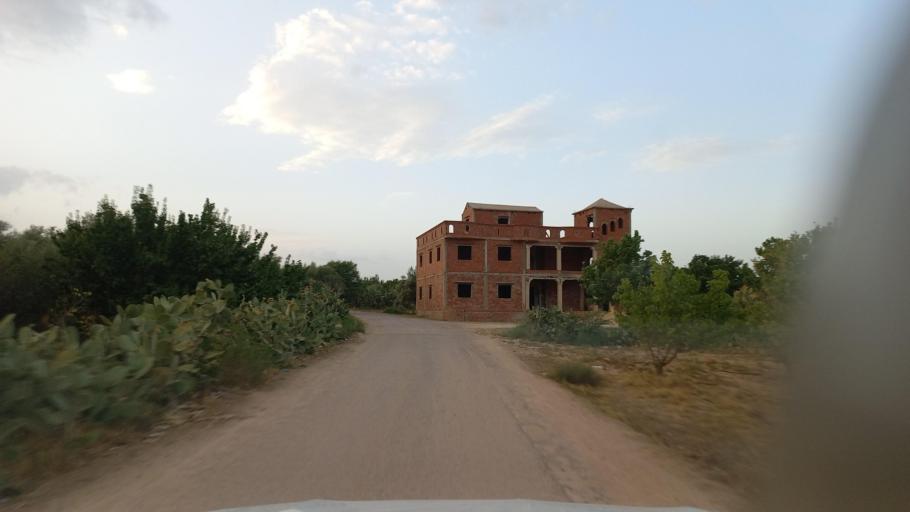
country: TN
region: Al Qasrayn
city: Kasserine
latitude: 35.2745
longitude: 9.0535
